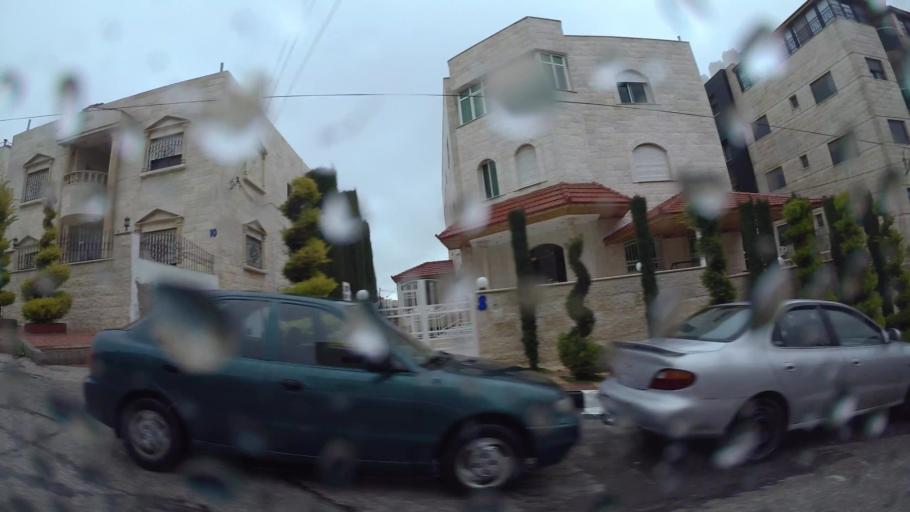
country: JO
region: Amman
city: Al Jubayhah
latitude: 32.0401
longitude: 35.8936
